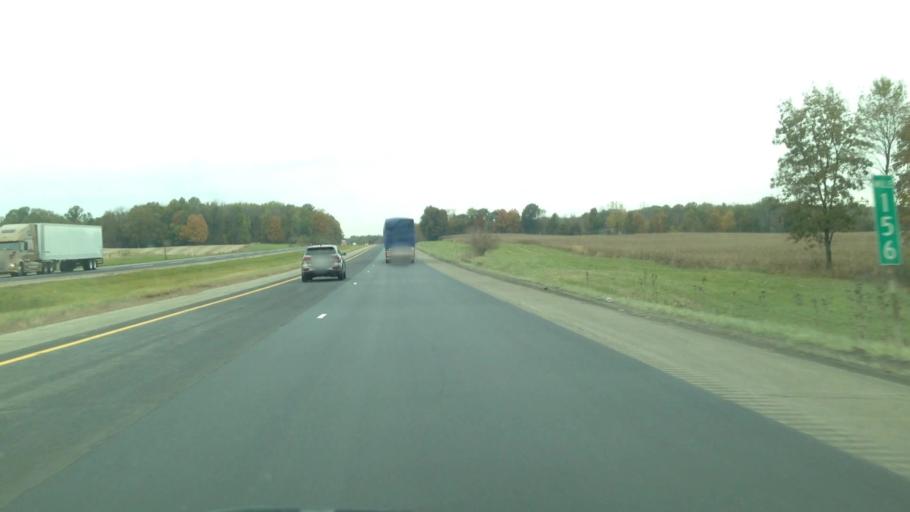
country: US
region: Indiana
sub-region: Steuben County
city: Hamilton
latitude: 41.6323
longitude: -84.8201
